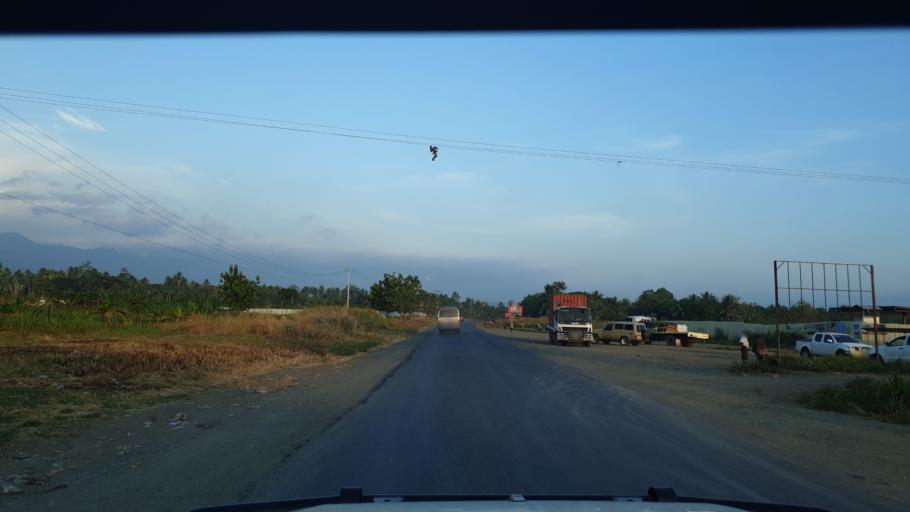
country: PG
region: Morobe
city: Lae
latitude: -6.5643
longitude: 146.7536
